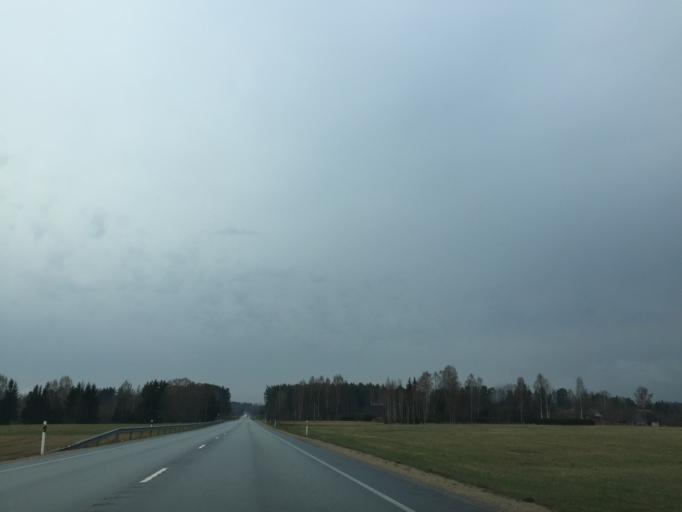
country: EE
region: Tartu
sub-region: UElenurme vald
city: Ulenurme
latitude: 58.2089
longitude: 26.7072
